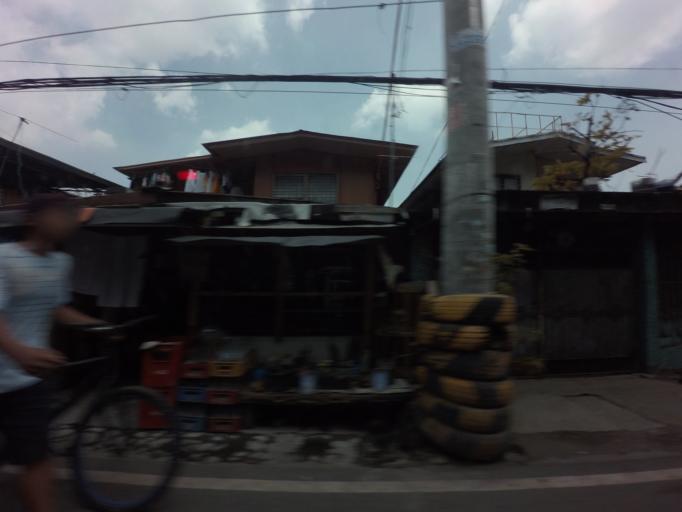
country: PH
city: Sambayanihan People's Village
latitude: 14.4484
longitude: 121.0511
